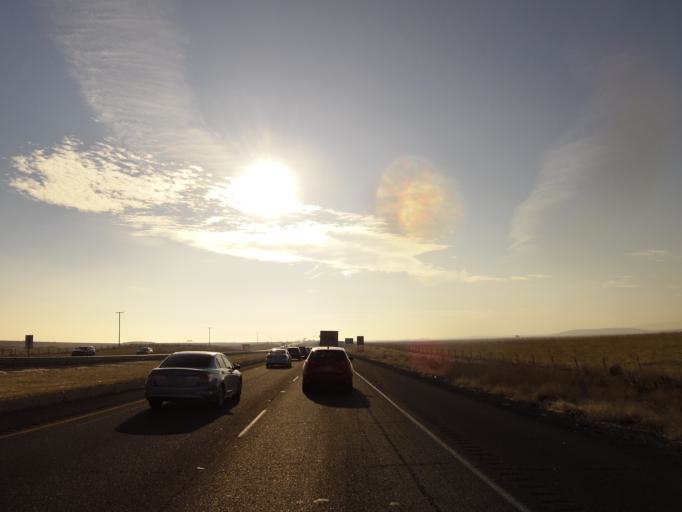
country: US
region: California
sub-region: Merced County
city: Los Banos
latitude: 37.0641
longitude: -120.9772
